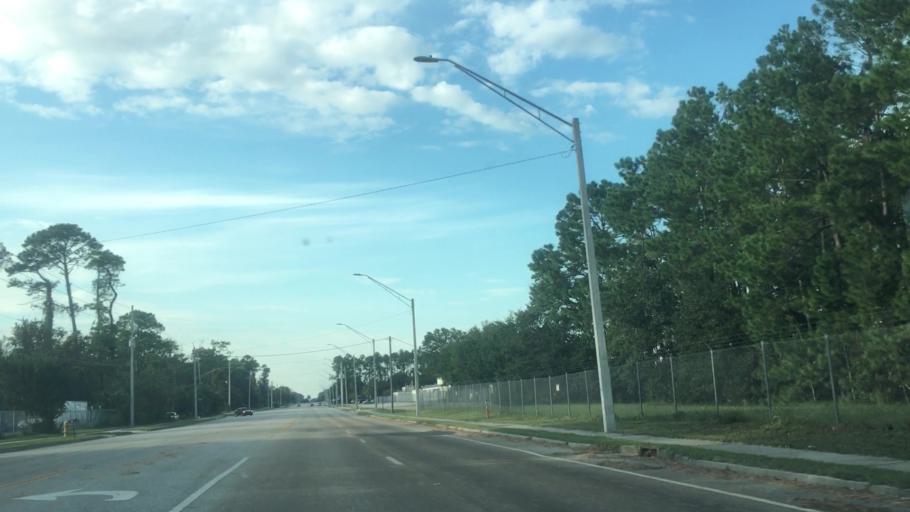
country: US
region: Florida
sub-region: Duval County
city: Atlantic Beach
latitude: 30.3287
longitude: -81.5231
